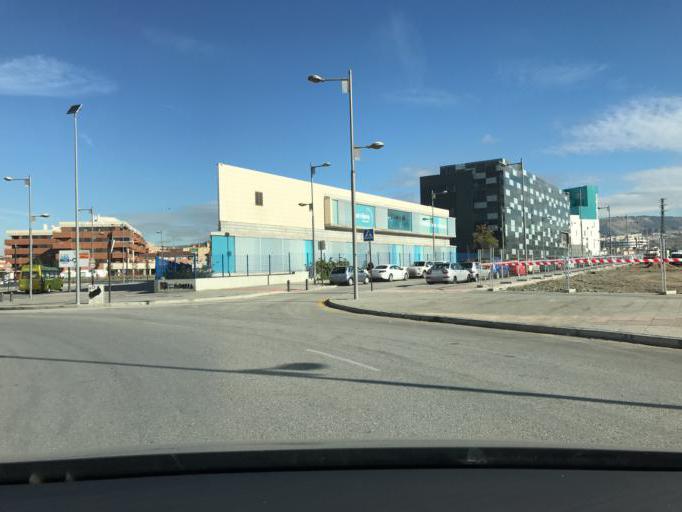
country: ES
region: Andalusia
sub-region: Provincia de Granada
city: Armilla
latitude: 37.1479
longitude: -3.5986
